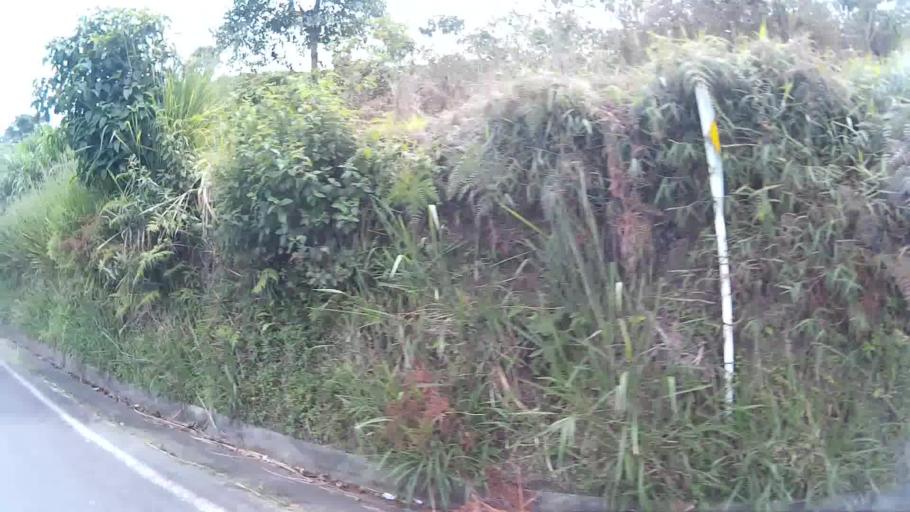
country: CO
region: Risaralda
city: Marsella
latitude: 4.9164
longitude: -75.7433
